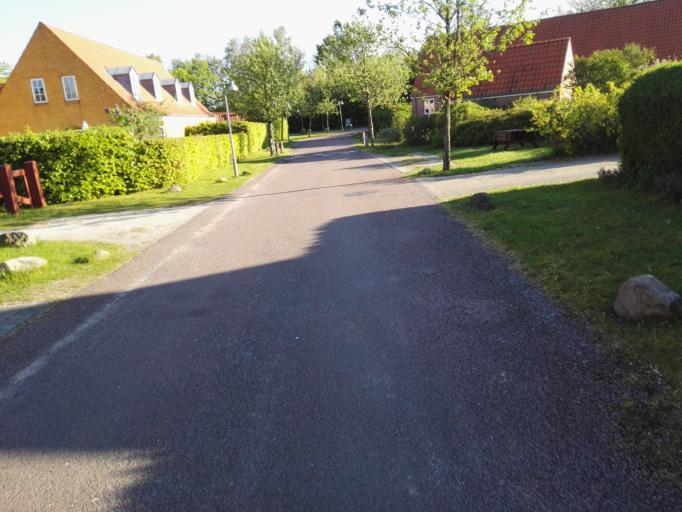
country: DK
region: Capital Region
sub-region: Ballerup Kommune
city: Ballerup
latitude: 55.7336
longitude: 12.3399
